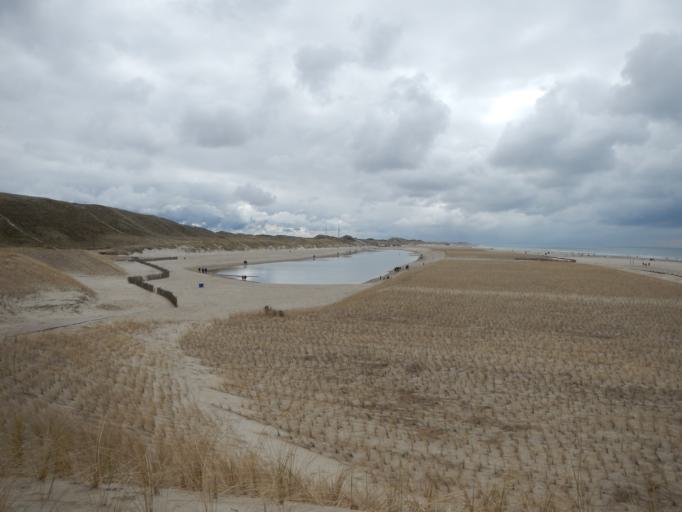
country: NL
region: North Holland
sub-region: Gemeente Bergen
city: Egmond aan Zee
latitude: 52.7250
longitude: 4.6383
